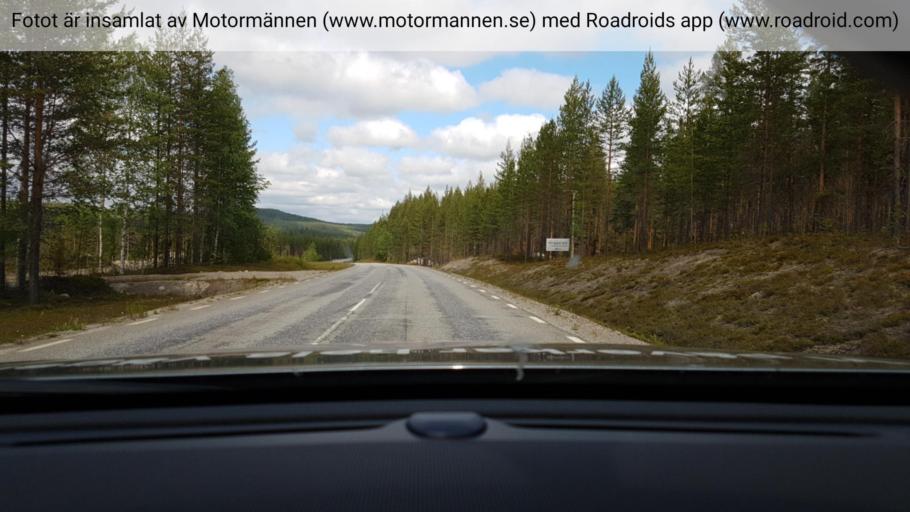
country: SE
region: Vaesterbotten
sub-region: Lycksele Kommun
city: Lycksele
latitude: 64.8552
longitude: 18.7420
